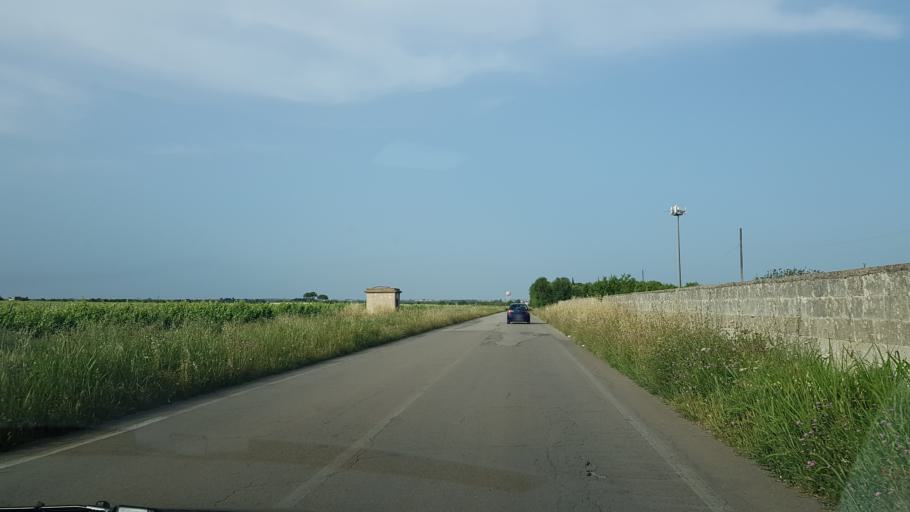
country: IT
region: Apulia
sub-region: Provincia di Brindisi
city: San Pancrazio Salentino
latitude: 40.4227
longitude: 17.8531
